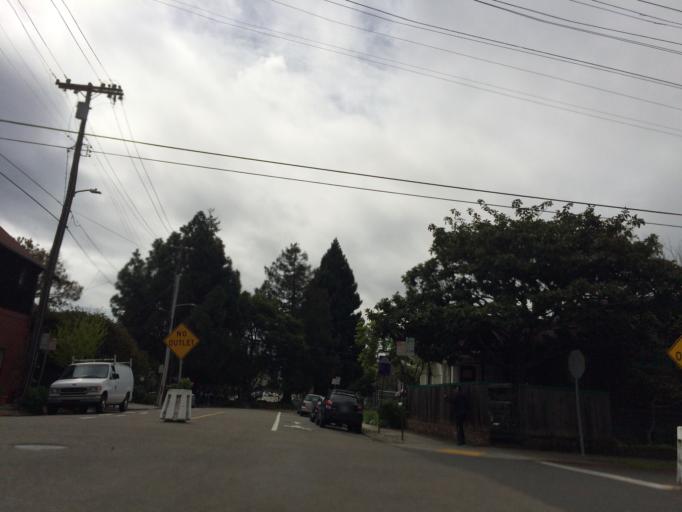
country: US
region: California
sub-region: Alameda County
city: Berkeley
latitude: 37.8735
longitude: -122.2801
